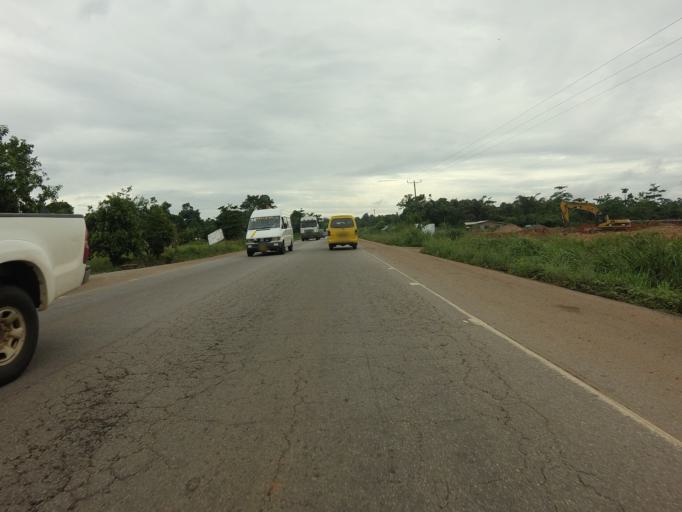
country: GH
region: Eastern
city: Nkawkaw
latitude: 6.4812
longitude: -0.6635
